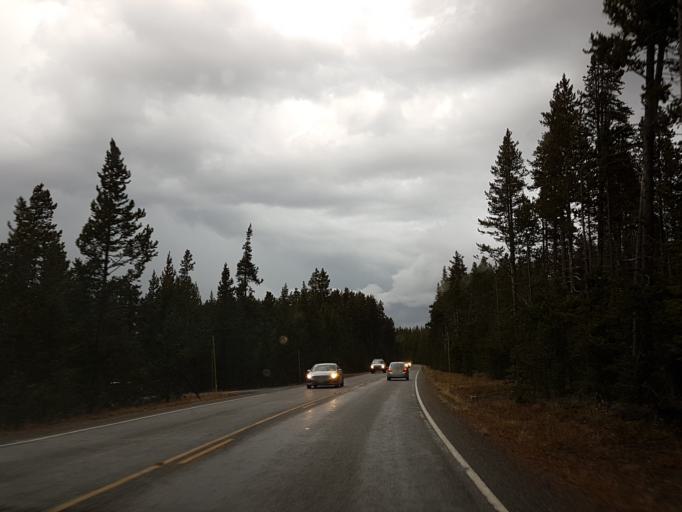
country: US
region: Montana
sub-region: Gallatin County
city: West Yellowstone
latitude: 44.4561
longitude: -110.5080
